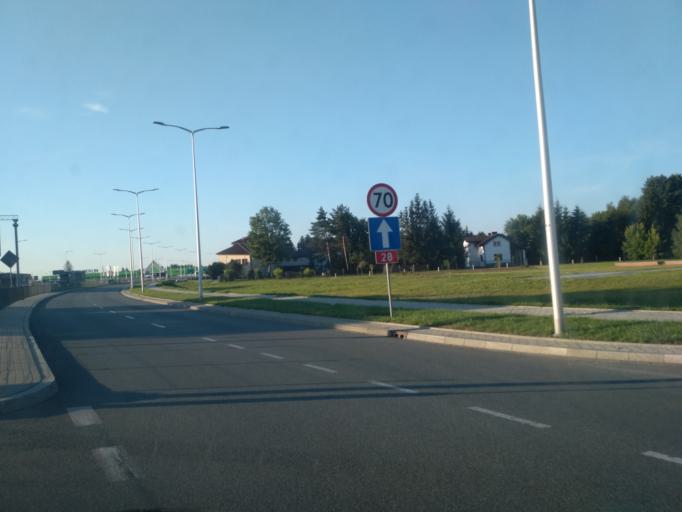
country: PL
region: Subcarpathian Voivodeship
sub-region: Krosno
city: Krosno
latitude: 49.6793
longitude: 21.7724
